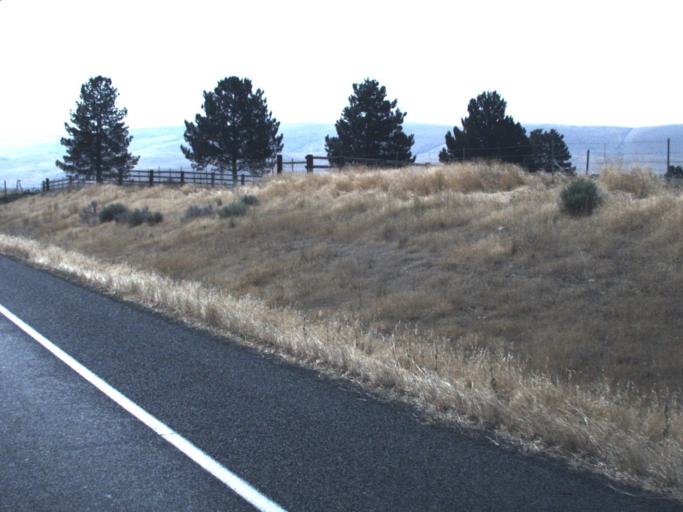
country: US
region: Washington
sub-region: Yakima County
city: Zillah
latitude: 46.5155
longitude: -120.2035
